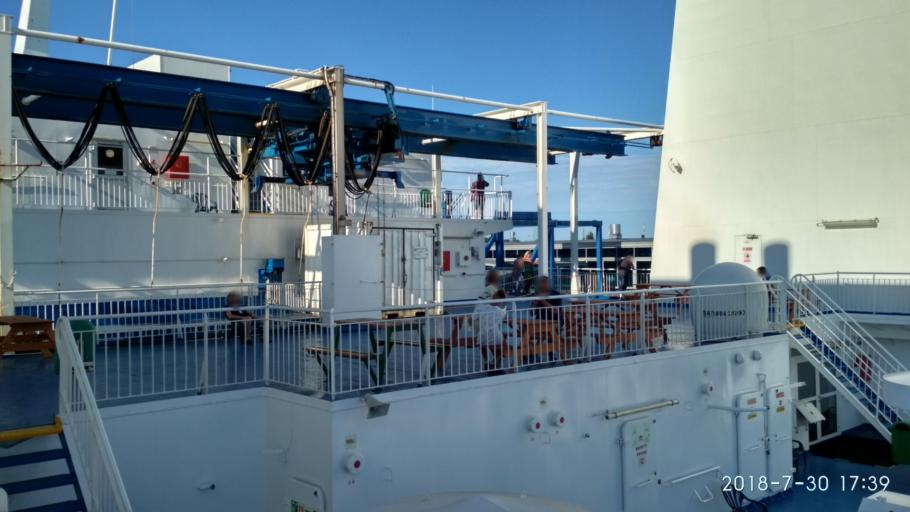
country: PL
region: West Pomeranian Voivodeship
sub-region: Swinoujscie
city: Swinoujscie
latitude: 53.8967
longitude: 14.2563
